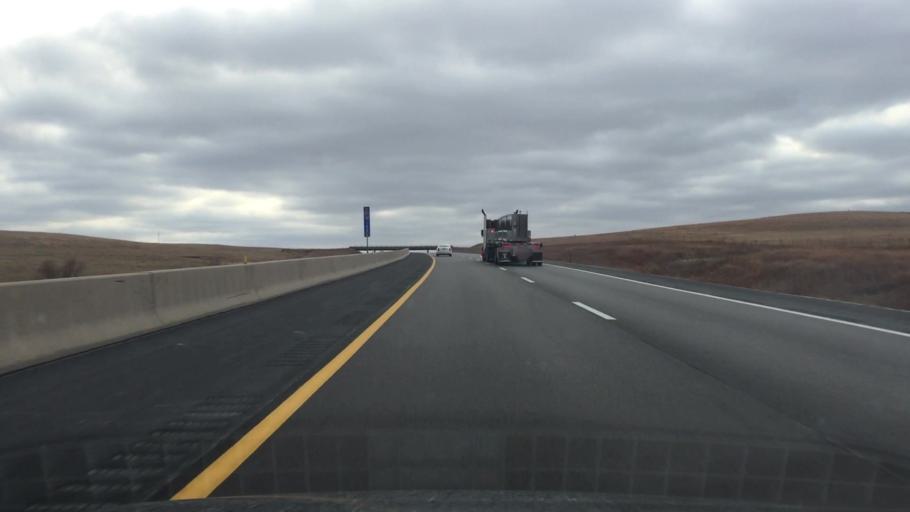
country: US
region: Kansas
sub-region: Chase County
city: Cottonwood Falls
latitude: 38.1651
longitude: -96.4809
